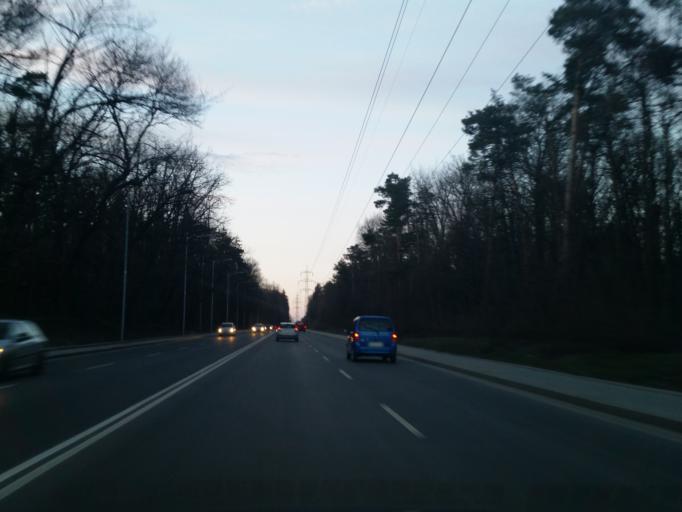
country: BG
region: Sofia-Capital
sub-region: Stolichna Obshtina
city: Sofia
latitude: 42.6677
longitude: 23.3376
